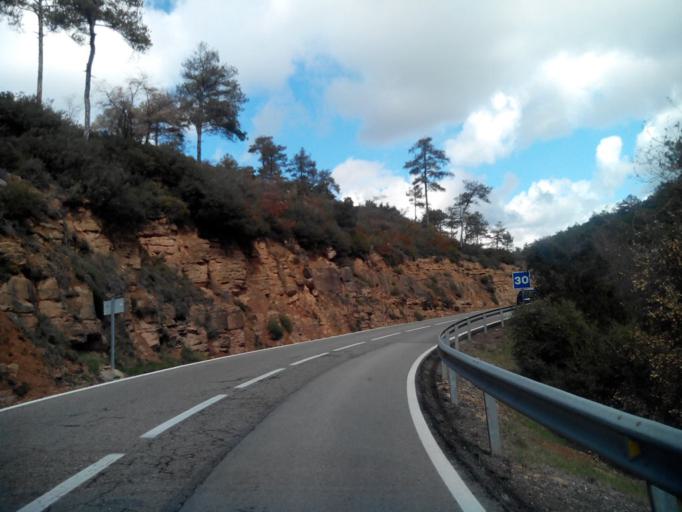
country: ES
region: Catalonia
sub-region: Provincia de Barcelona
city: Cardona
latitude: 41.9420
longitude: 1.6965
